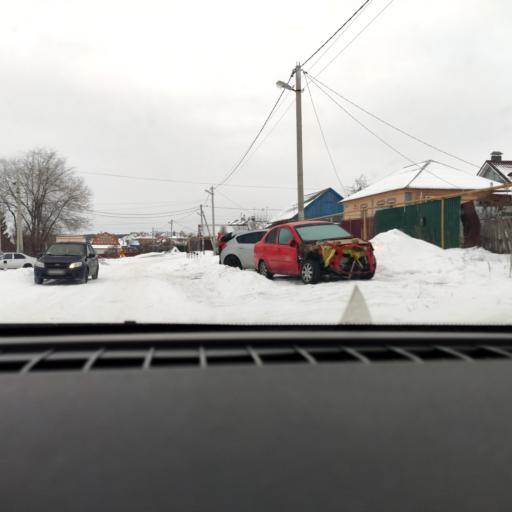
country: RU
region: Voronezj
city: Maslovka
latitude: 51.5429
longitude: 39.2300
